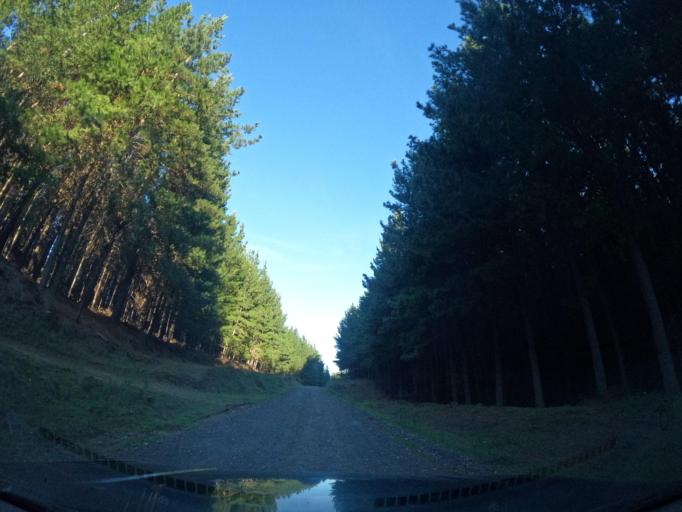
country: CL
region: Biobio
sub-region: Provincia de Concepcion
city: Chiguayante
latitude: -37.0845
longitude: -72.9101
